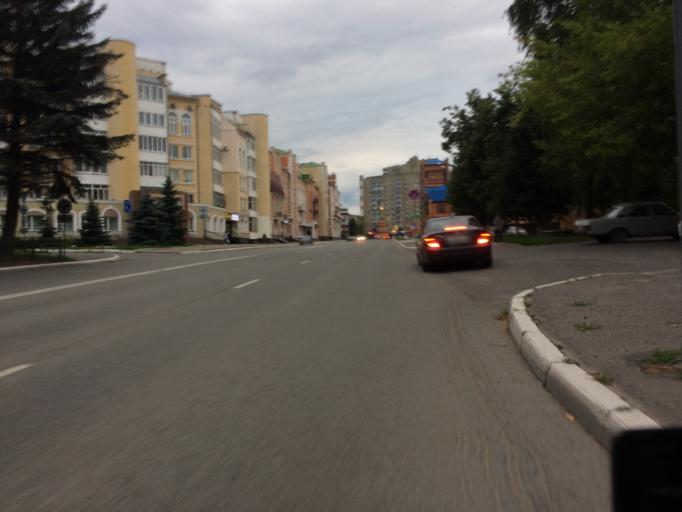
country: RU
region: Mariy-El
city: Yoshkar-Ola
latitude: 56.6293
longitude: 47.8863
